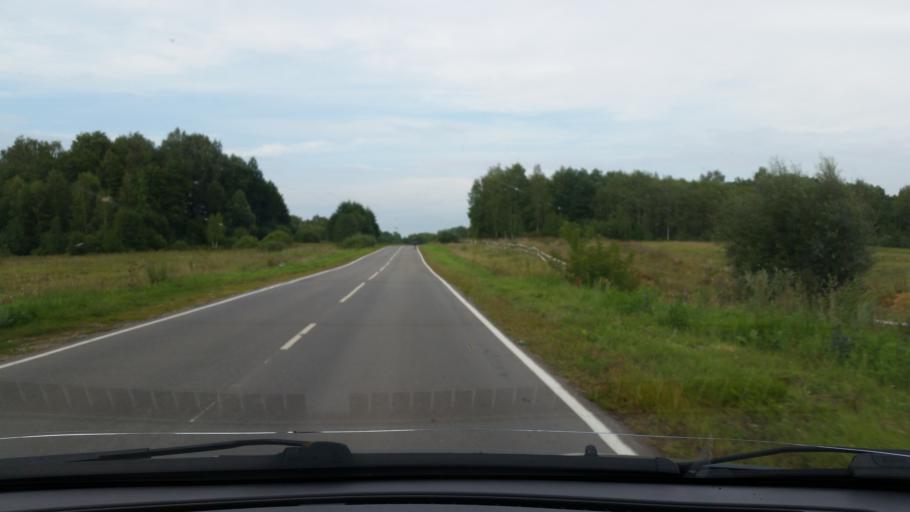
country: RU
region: Moskovskaya
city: Bol'shoye Gryzlovo
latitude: 54.8489
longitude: 37.7305
